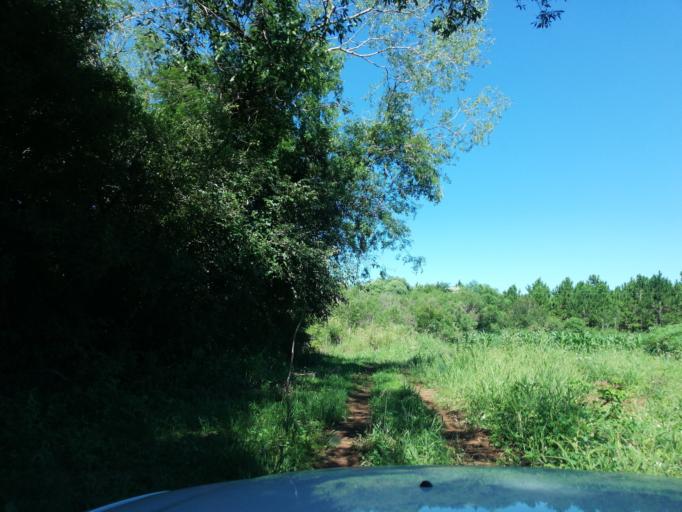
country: AR
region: Misiones
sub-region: Departamento de Leandro N. Alem
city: Leandro N. Alem
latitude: -27.5771
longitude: -55.3733
